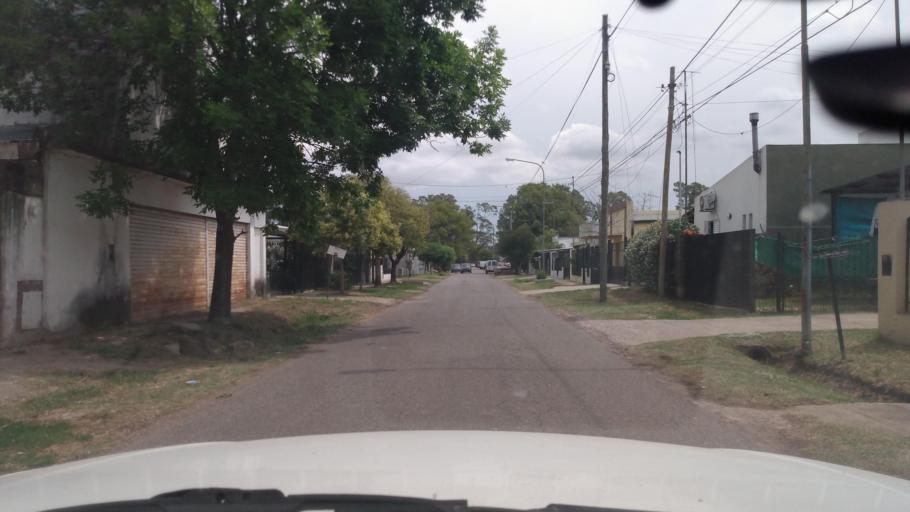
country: AR
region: Buenos Aires
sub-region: Partido de Lujan
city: Lujan
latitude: -34.5567
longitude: -59.2058
